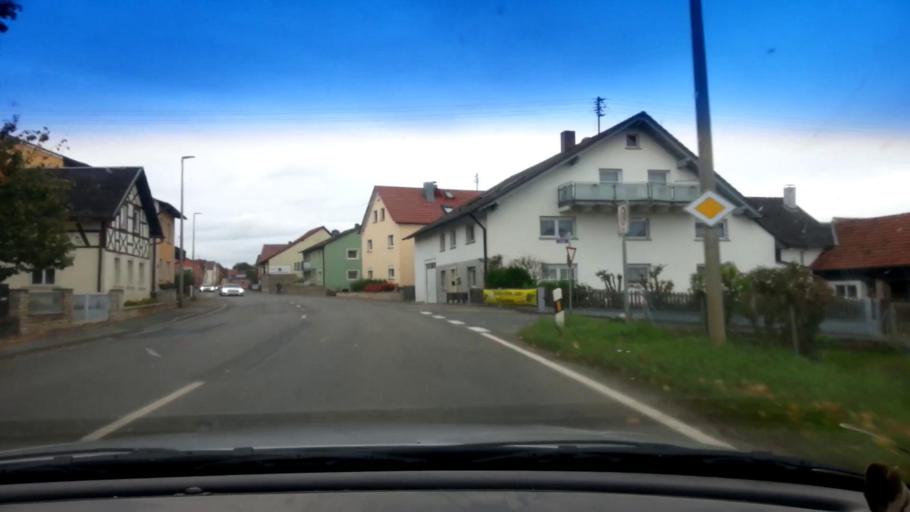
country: DE
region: Bavaria
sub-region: Upper Franconia
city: Reckendorf
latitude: 50.0165
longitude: 10.8276
